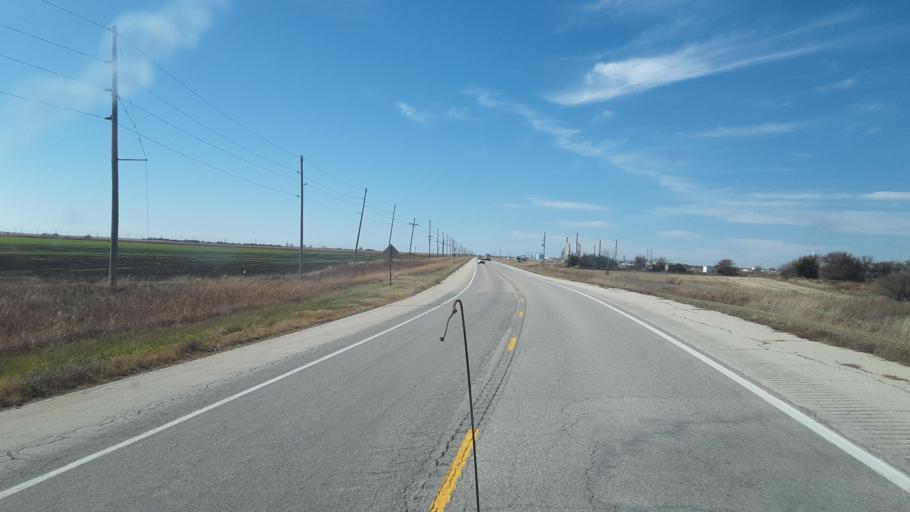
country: US
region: Kansas
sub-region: McPherson County
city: Inman
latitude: 38.3771
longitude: -97.8204
